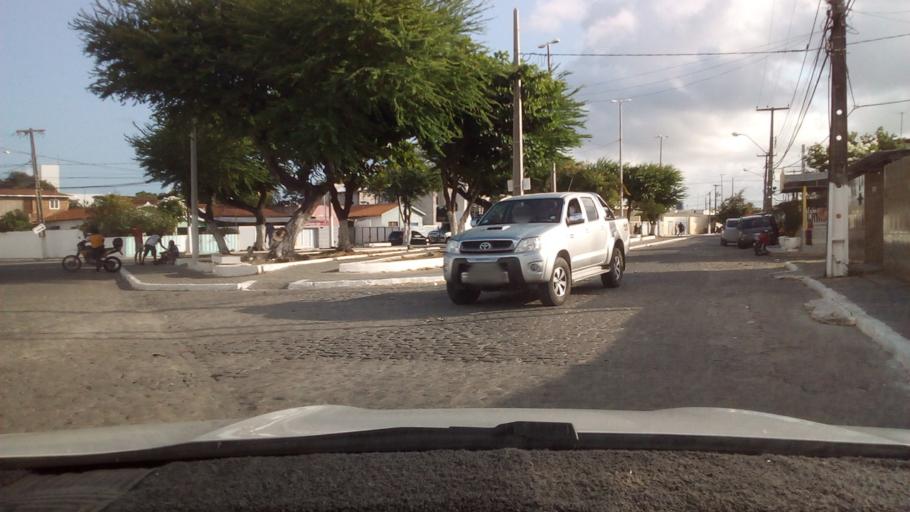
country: BR
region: Paraiba
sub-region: Cabedelo
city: Cabedelo
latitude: -6.9702
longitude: -34.8336
